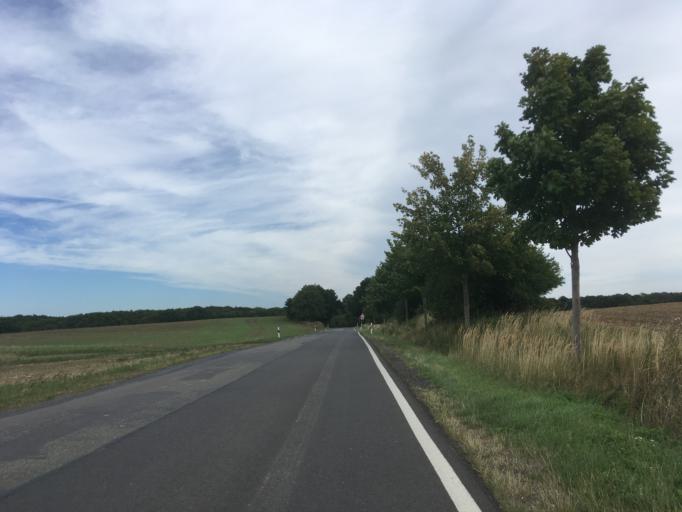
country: DE
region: Brandenburg
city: Mittenwalde
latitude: 53.2370
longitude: 13.5867
